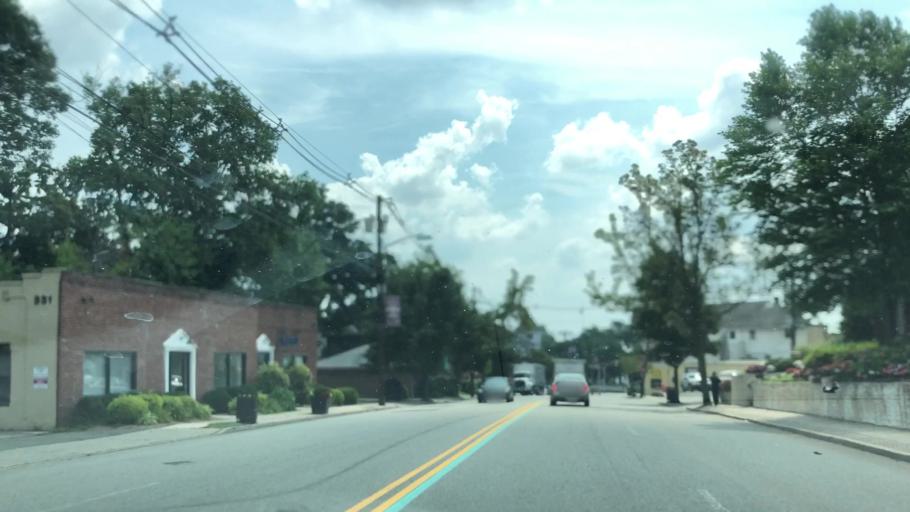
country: US
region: New Jersey
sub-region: Essex County
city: West Orange
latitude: 40.7894
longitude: -74.2319
